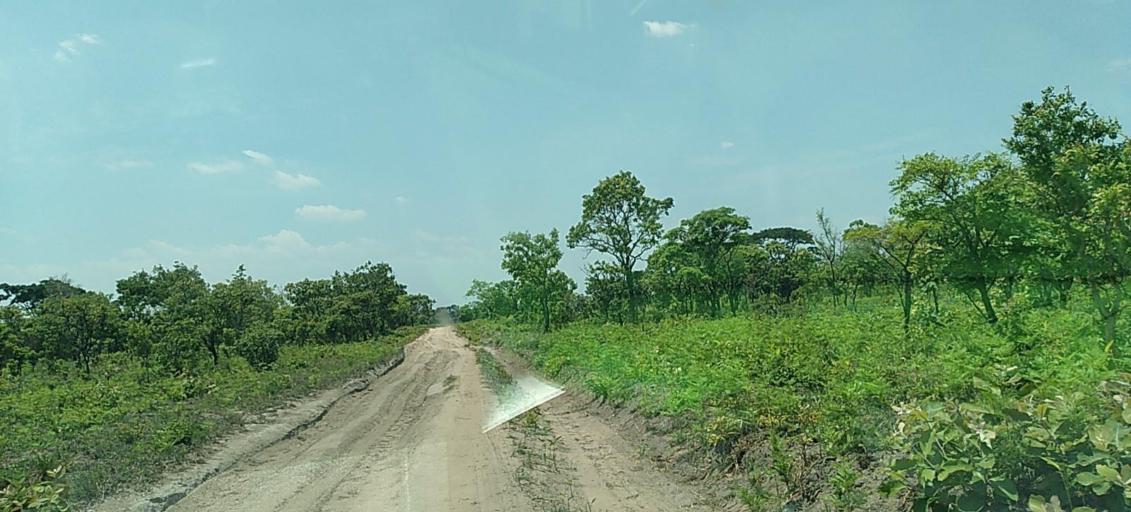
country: CD
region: Katanga
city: Kolwezi
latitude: -11.3367
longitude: 25.2235
